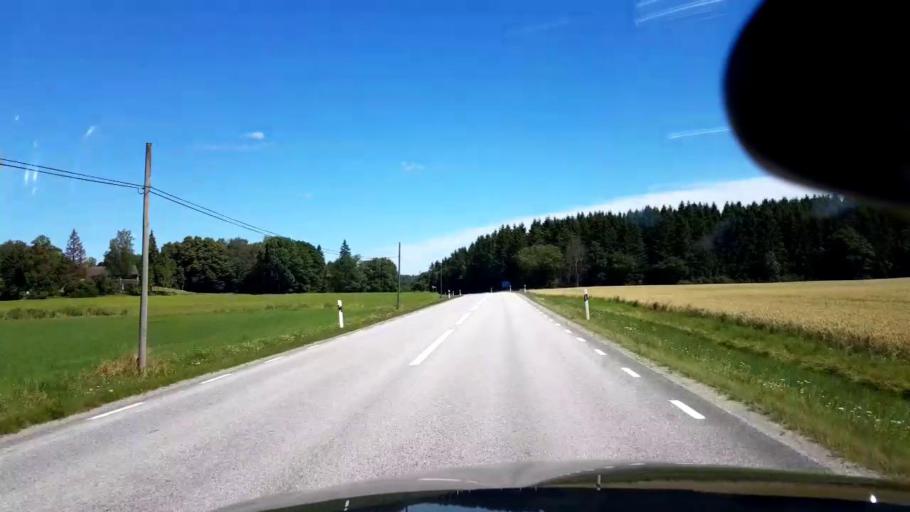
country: SE
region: Uppsala
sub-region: Habo Kommun
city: Balsta
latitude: 59.6329
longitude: 17.6022
